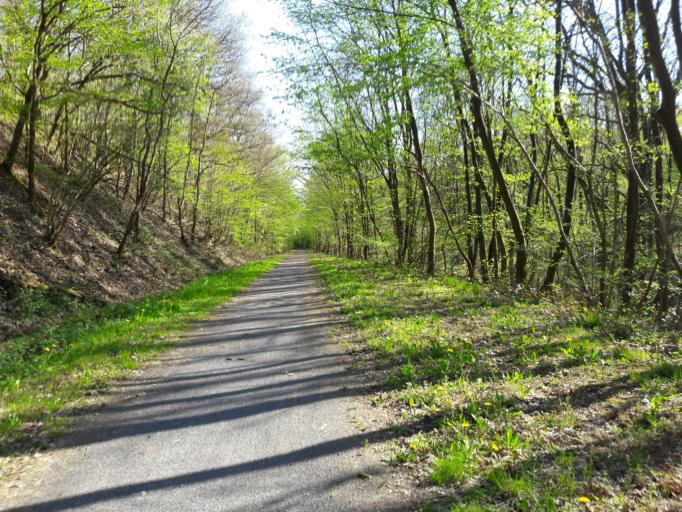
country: FR
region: Nord-Pas-de-Calais
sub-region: Departement du Nord
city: Sains-du-Nord
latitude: 50.1364
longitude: 4.0662
